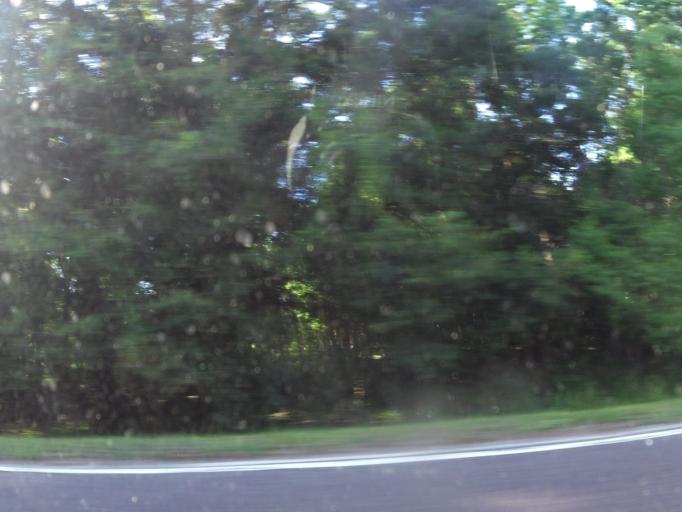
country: US
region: Florida
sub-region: Nassau County
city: Nassau Village-Ratliff
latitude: 30.4664
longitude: -81.8039
